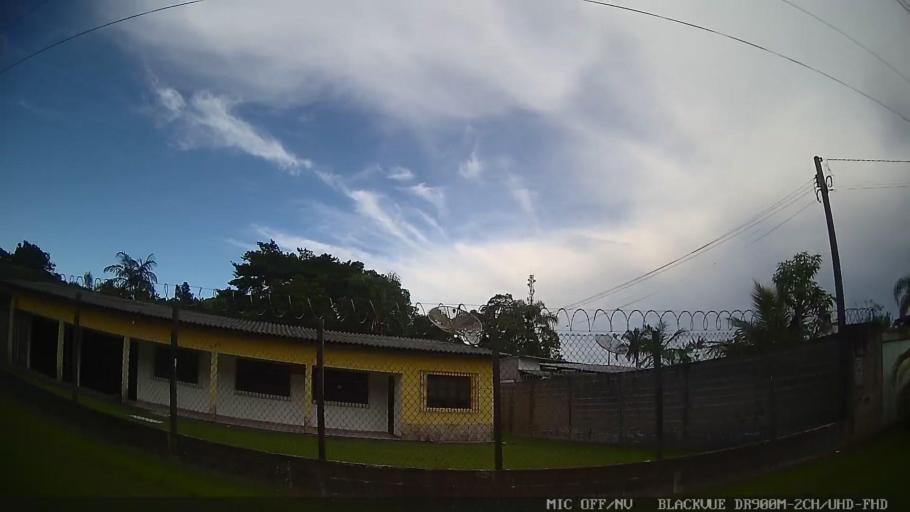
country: BR
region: Sao Paulo
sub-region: Iguape
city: Iguape
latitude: -24.6831
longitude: -47.4667
